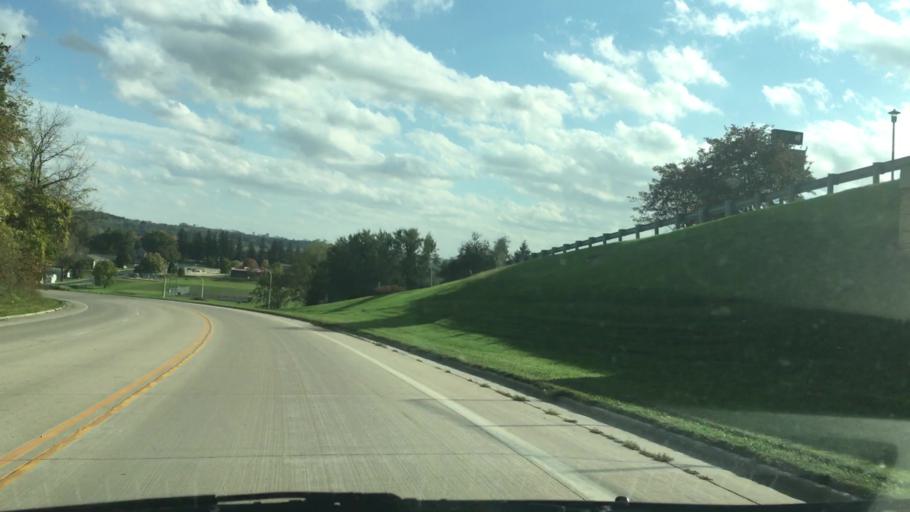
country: US
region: Minnesota
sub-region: Fillmore County
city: Preston
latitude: 43.6811
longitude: -92.0914
